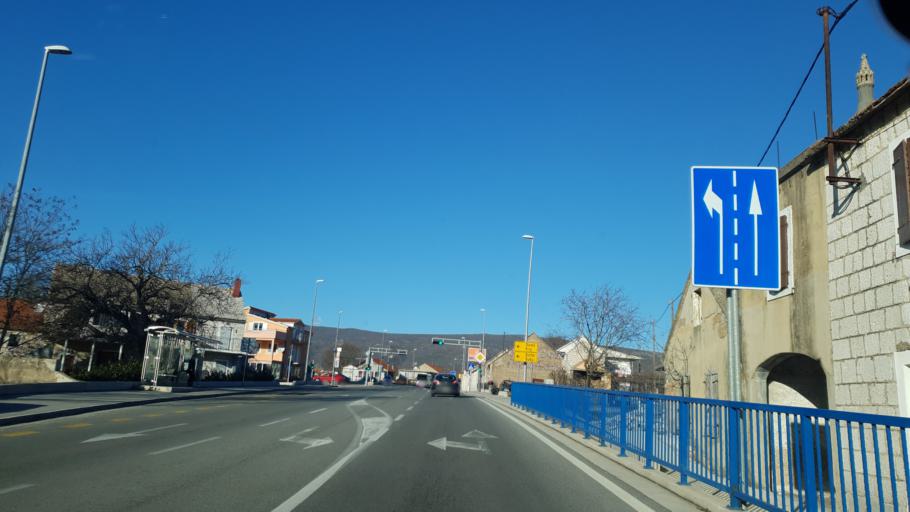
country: HR
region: Splitsko-Dalmatinska
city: Dugopolje
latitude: 43.6345
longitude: 16.5956
